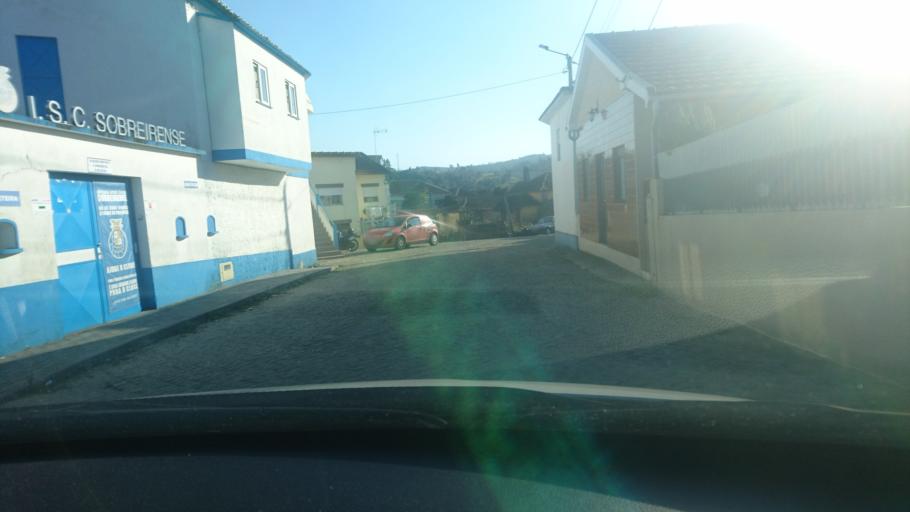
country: PT
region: Porto
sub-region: Paredes
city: Recarei
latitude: 41.1455
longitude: -8.3867
